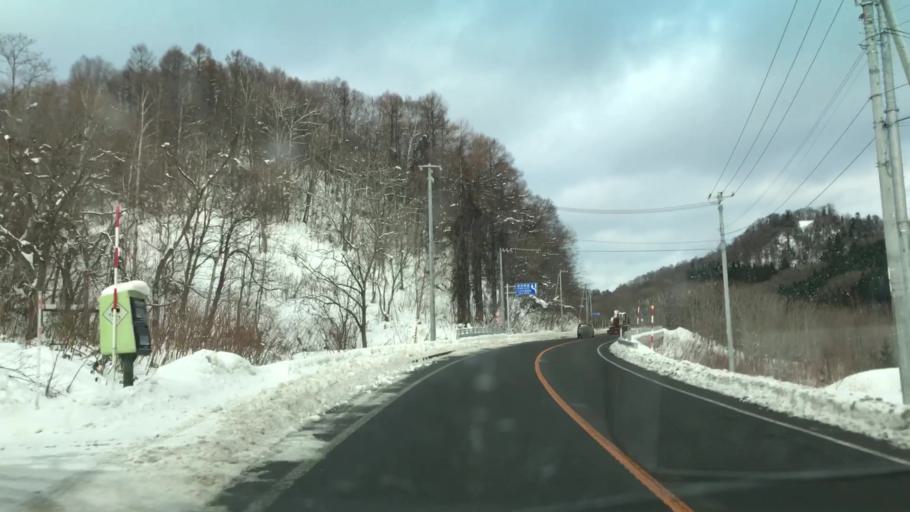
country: JP
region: Hokkaido
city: Yoichi
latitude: 43.2119
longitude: 140.7497
